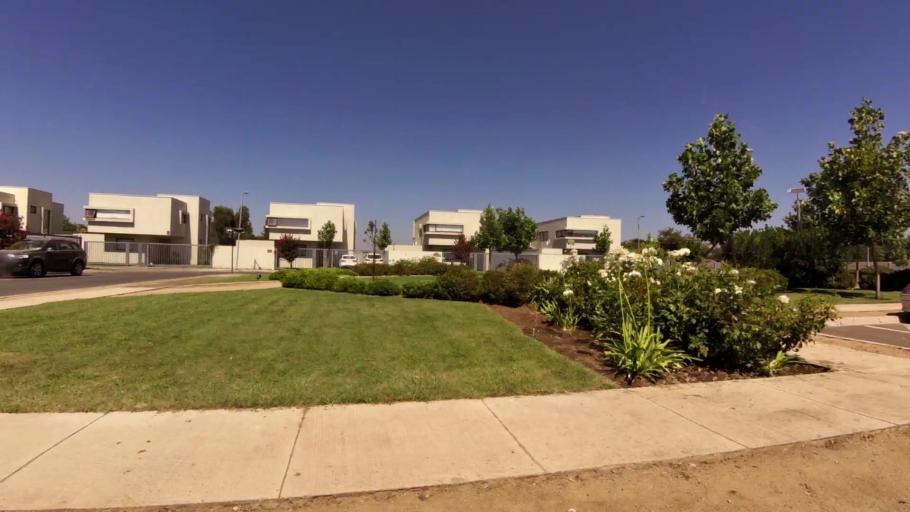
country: CL
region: Maule
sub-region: Provincia de Talca
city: Talca
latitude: -35.4302
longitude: -71.6100
